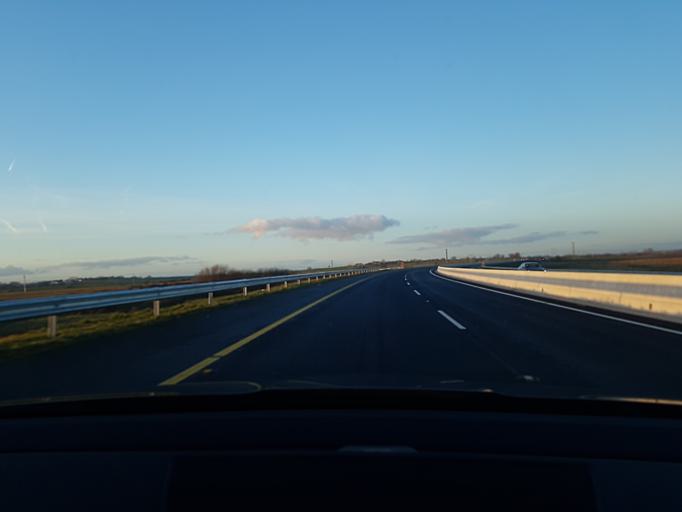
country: IE
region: Connaught
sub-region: County Galway
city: Tuam
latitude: 53.4701
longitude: -8.8633
